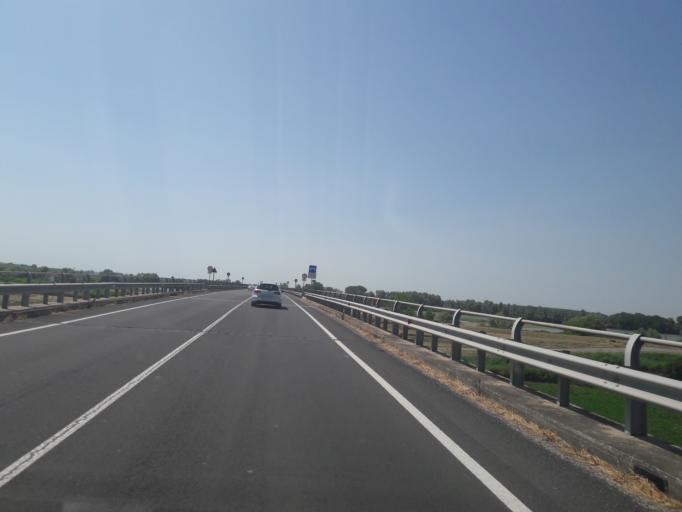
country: IT
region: Veneto
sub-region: Provincia di Rovigo
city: Bottrighe
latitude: 45.0260
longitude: 12.0989
